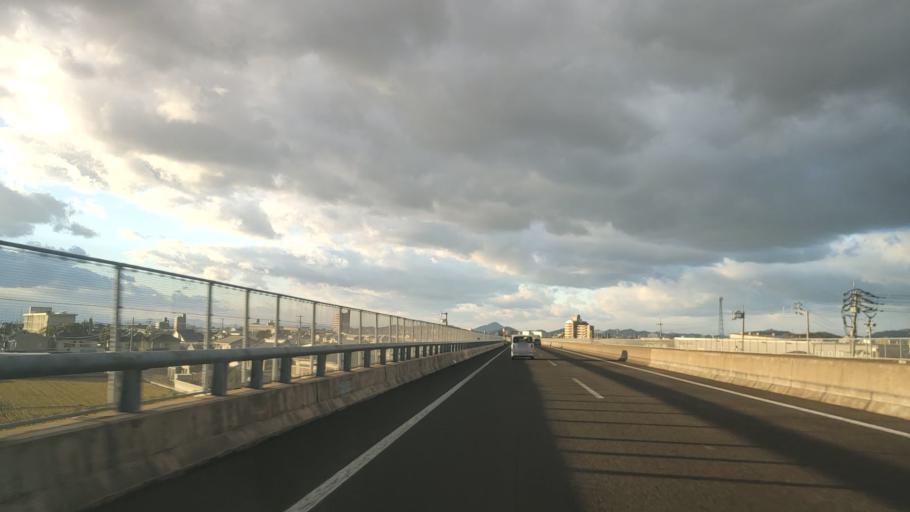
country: JP
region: Ehime
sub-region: Shikoku-chuo Shi
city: Matsuyama
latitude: 33.7925
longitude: 132.8018
